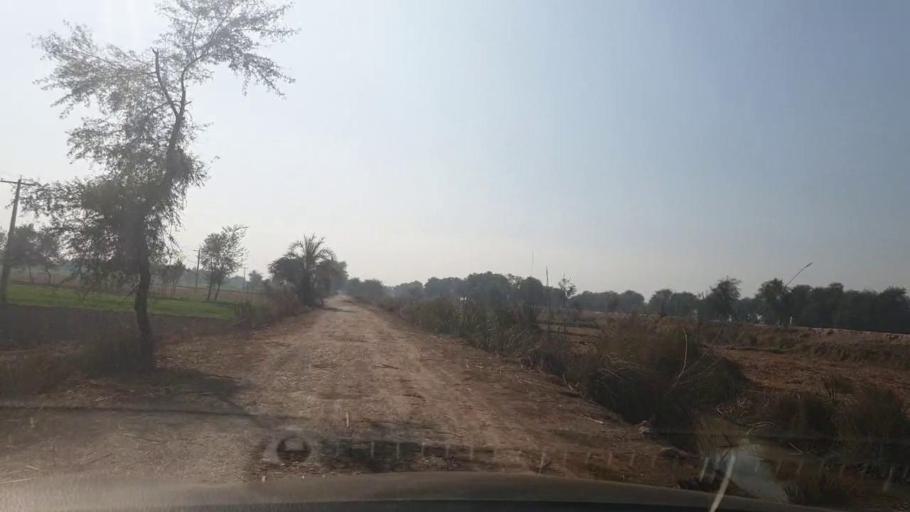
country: PK
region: Sindh
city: Ubauro
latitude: 28.1420
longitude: 69.6864
